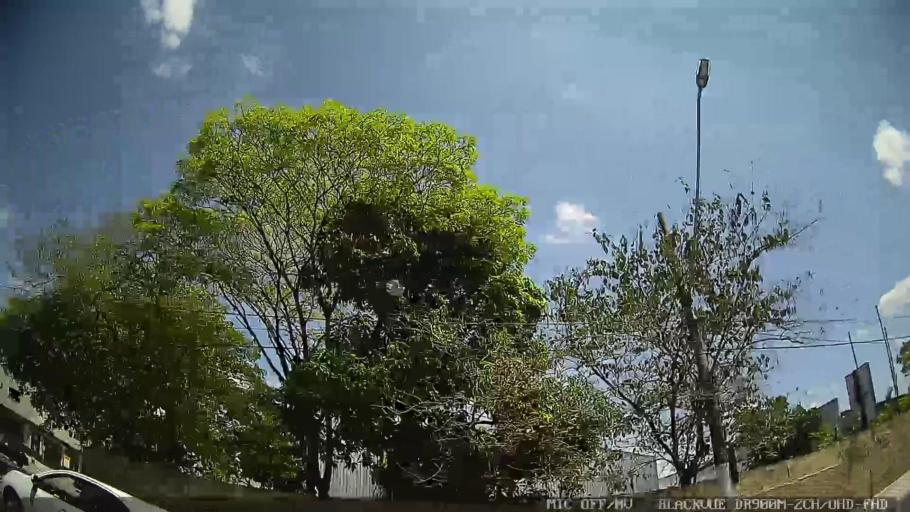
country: BR
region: Sao Paulo
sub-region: Guarulhos
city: Guarulhos
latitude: -23.5143
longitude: -46.5433
